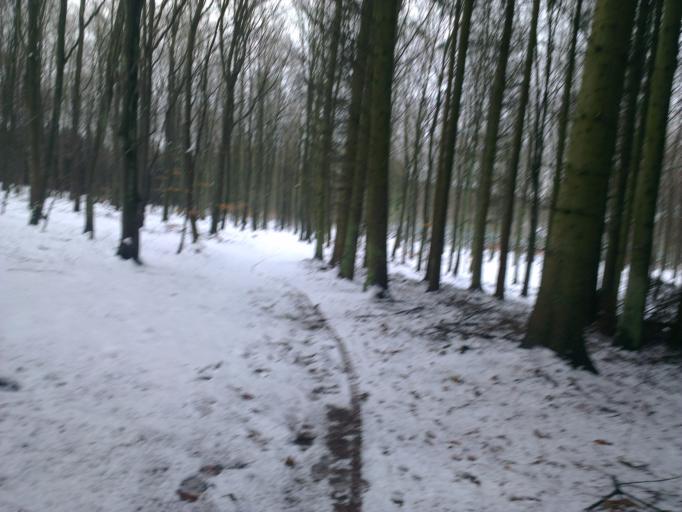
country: DK
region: Capital Region
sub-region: Frederikssund Kommune
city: Jaegerspris
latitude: 55.8446
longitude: 12.0178
